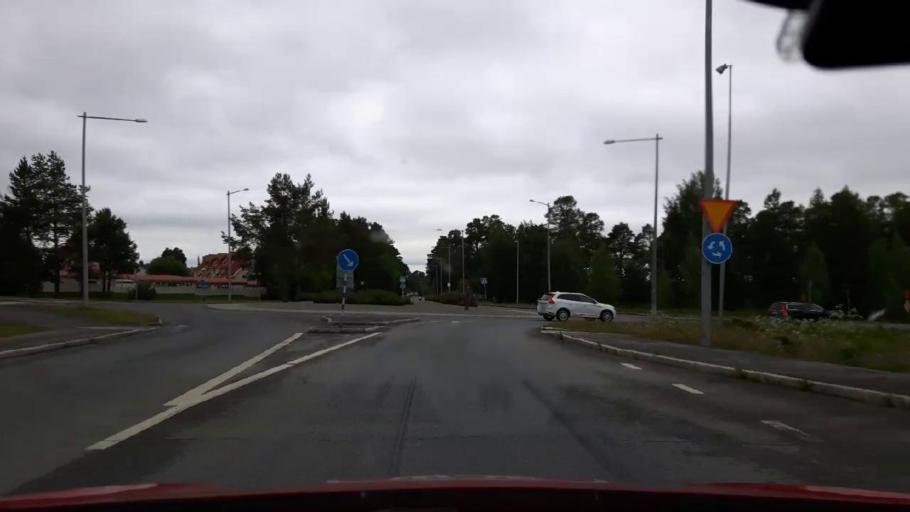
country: SE
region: Jaemtland
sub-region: OEstersunds Kommun
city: Ostersund
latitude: 63.1878
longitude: 14.6516
